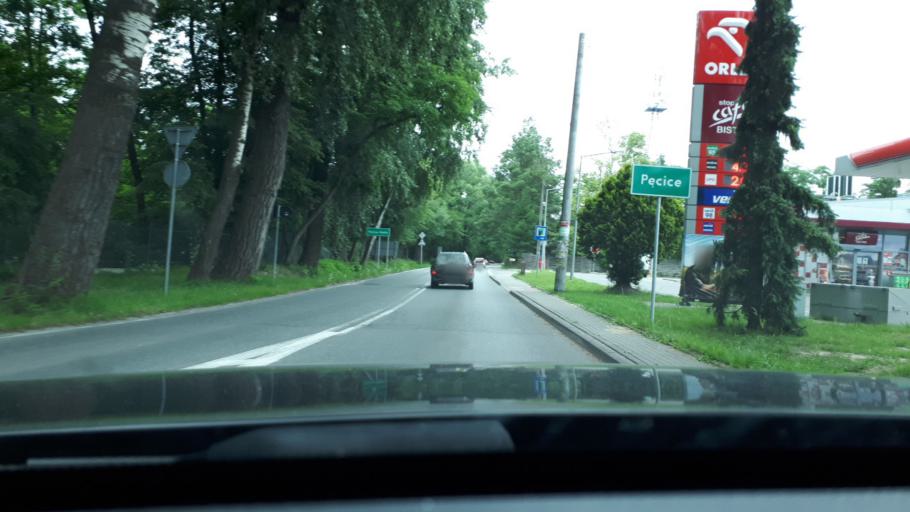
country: PL
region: Masovian Voivodeship
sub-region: Powiat pruszkowski
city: Komorow
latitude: 52.1445
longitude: 20.8476
